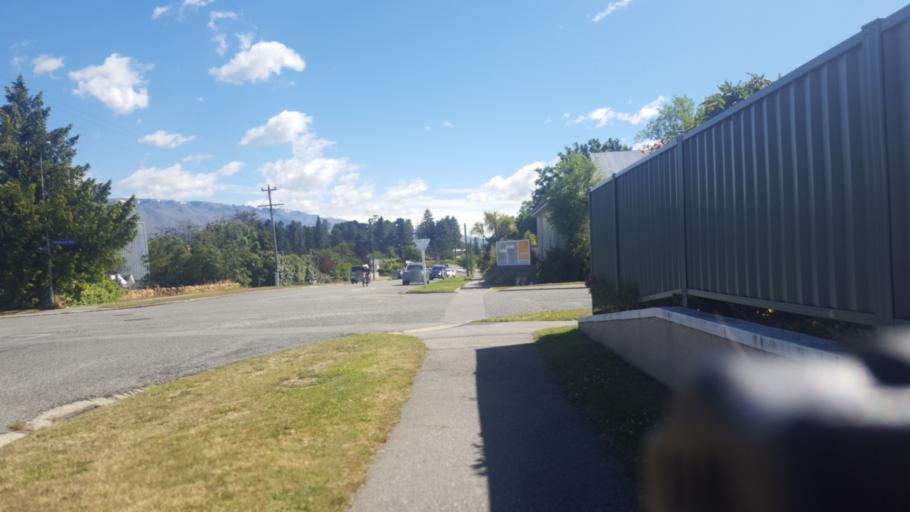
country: NZ
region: Otago
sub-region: Queenstown-Lakes District
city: Wanaka
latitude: -45.0465
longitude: 169.2084
